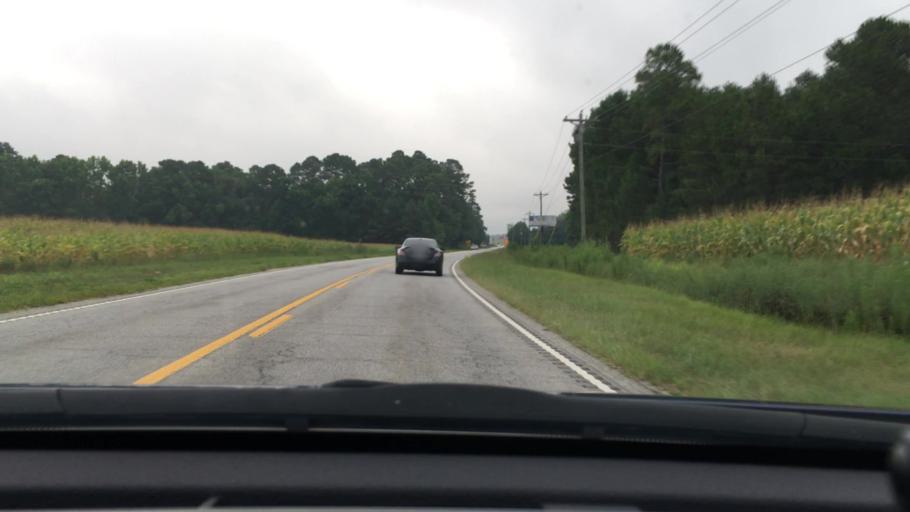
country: US
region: South Carolina
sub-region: Florence County
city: Timmonsville
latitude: 34.1977
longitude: -80.0380
